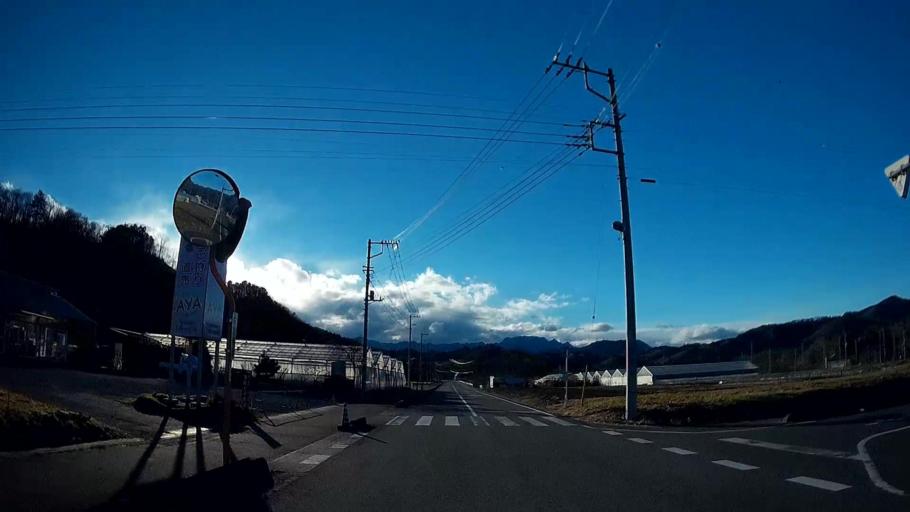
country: JP
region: Saitama
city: Chichibu
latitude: 36.0377
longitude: 139.0274
